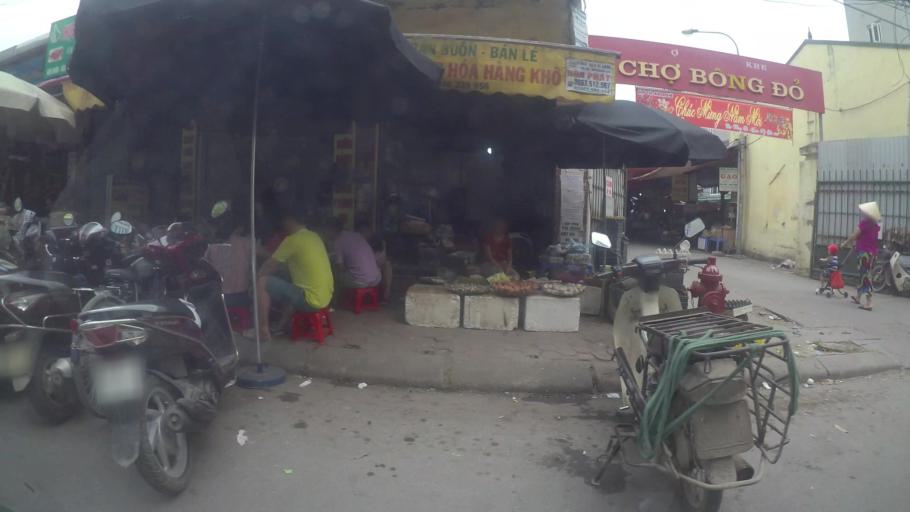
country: VN
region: Ha Noi
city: Ha Dong
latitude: 20.9669
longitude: 105.7662
